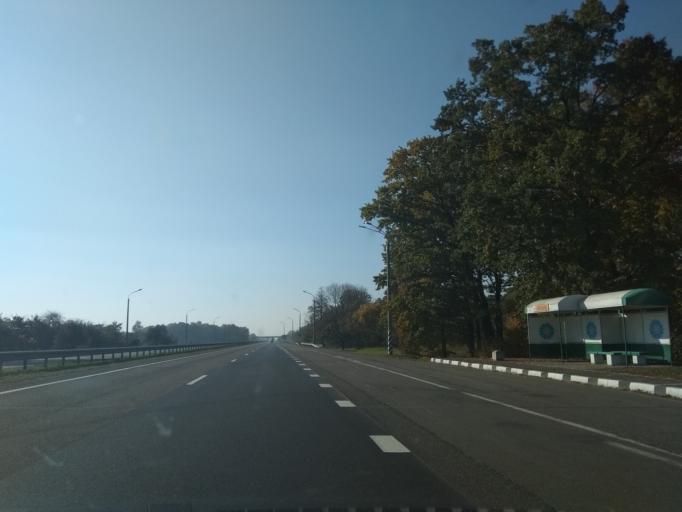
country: BY
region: Brest
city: Horad Kobryn
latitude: 52.1848
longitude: 24.3857
